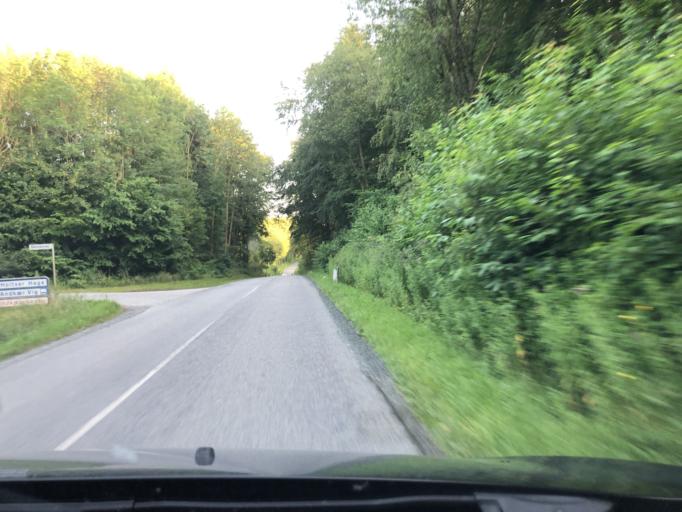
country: DK
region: South Denmark
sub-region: Vejle Kommune
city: Borkop
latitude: 55.6795
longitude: 9.6155
